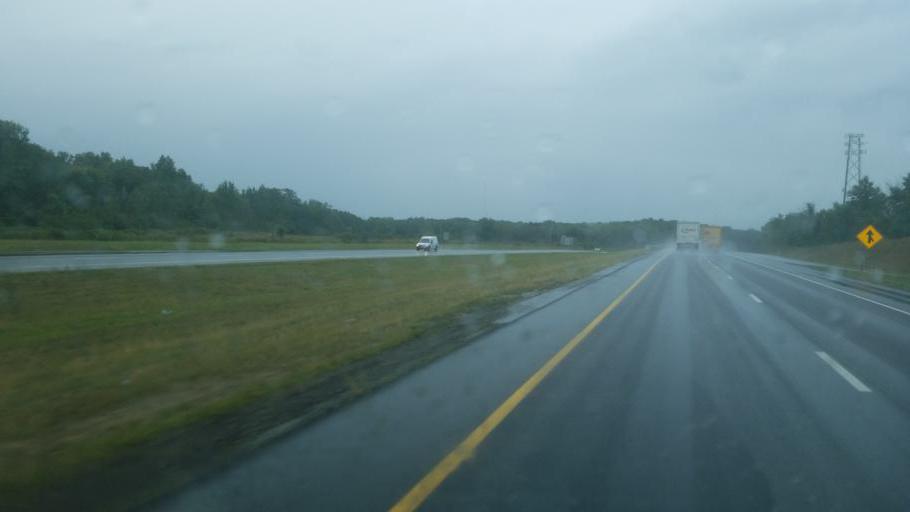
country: US
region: Ohio
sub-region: Summit County
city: Peninsula
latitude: 41.2433
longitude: -81.5913
